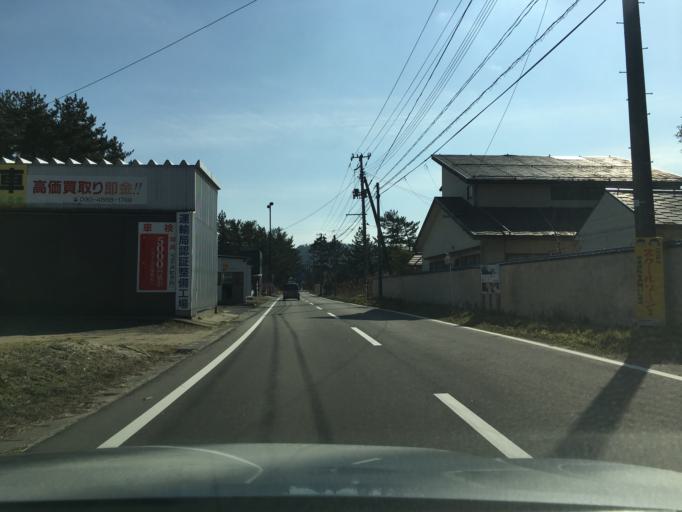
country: JP
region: Yamagata
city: Tsuruoka
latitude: 38.7961
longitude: 139.7698
